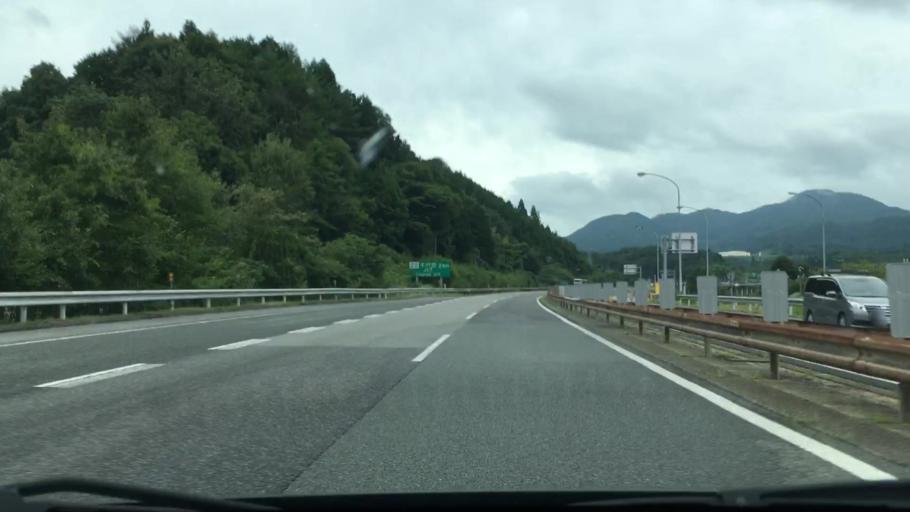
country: JP
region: Hiroshima
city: Hiroshima-shi
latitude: 34.6713
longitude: 132.5419
